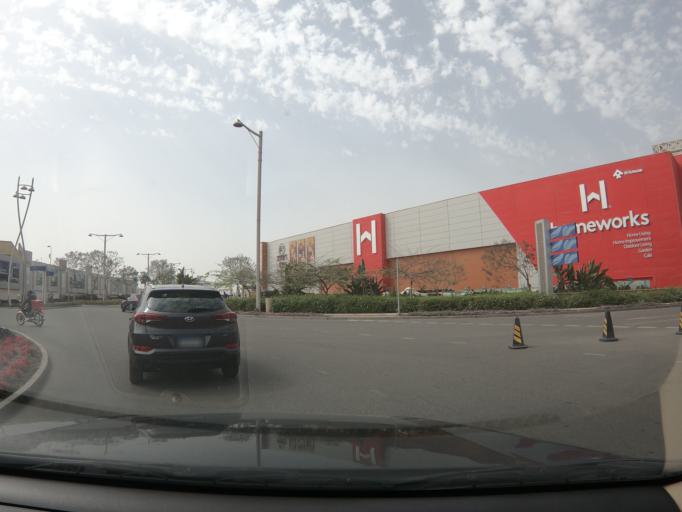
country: EG
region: Muhafazat al Qahirah
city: Cairo
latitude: 30.0305
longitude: 31.4063
